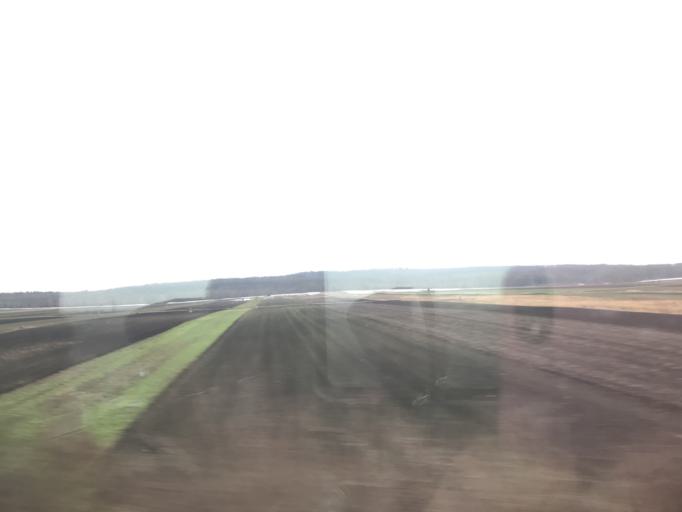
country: AT
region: Burgenland
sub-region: Politischer Bezirk Neusiedl am See
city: Parndorf
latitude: 48.0074
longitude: 16.8224
